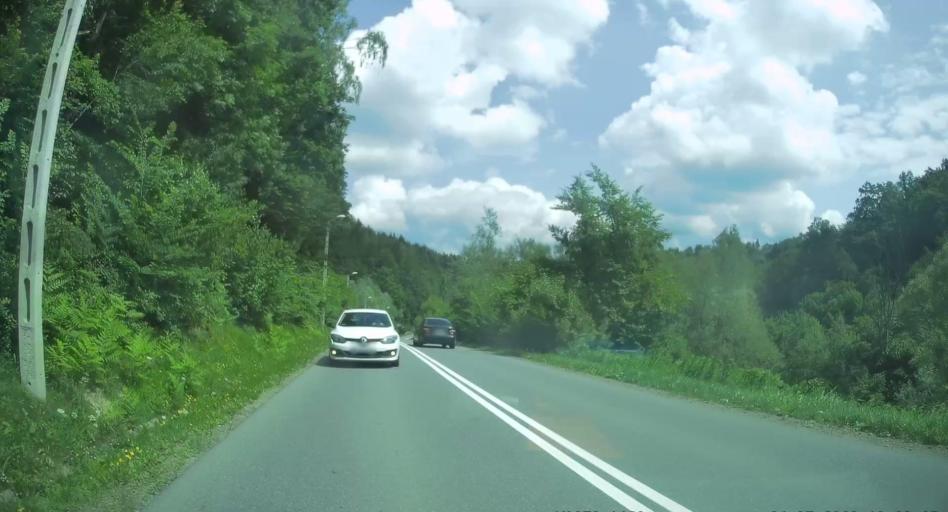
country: PL
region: Lesser Poland Voivodeship
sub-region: Powiat nowosadecki
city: Nowy Sacz
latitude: 49.6449
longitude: 20.7180
